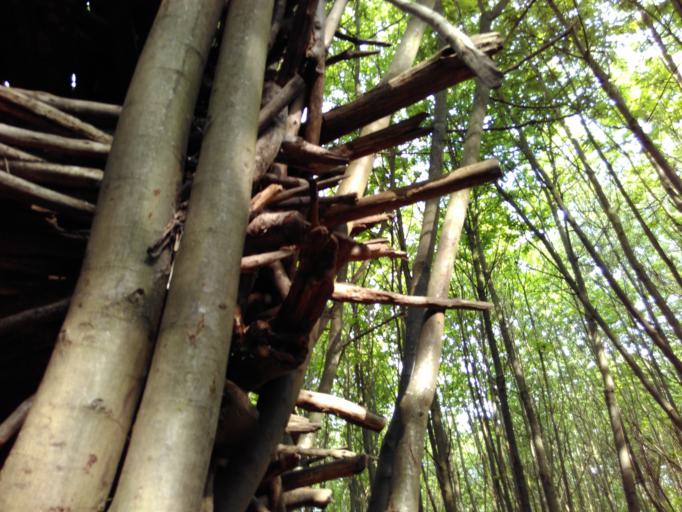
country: GB
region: England
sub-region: Suffolk
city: Ipswich
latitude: 52.0203
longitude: 1.1276
